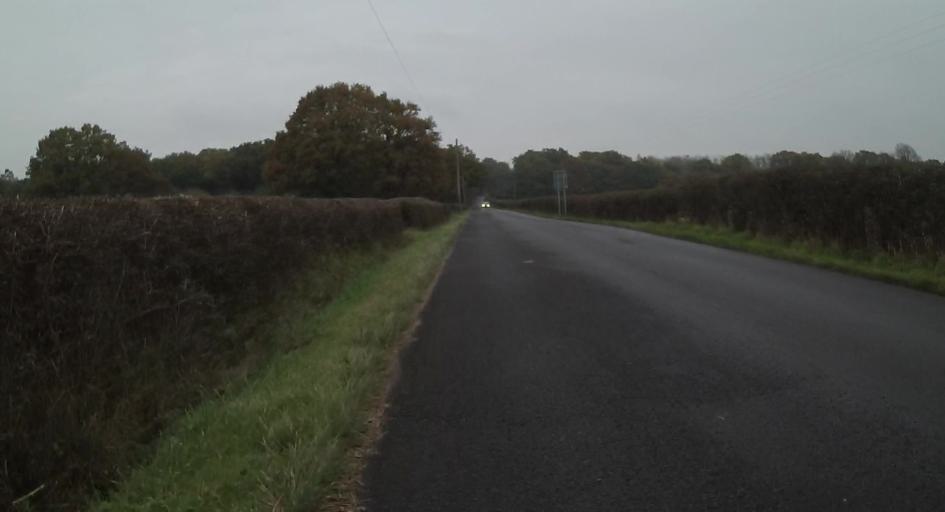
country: GB
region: England
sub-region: Hampshire
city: Kingsley
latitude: 51.1677
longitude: -0.8578
